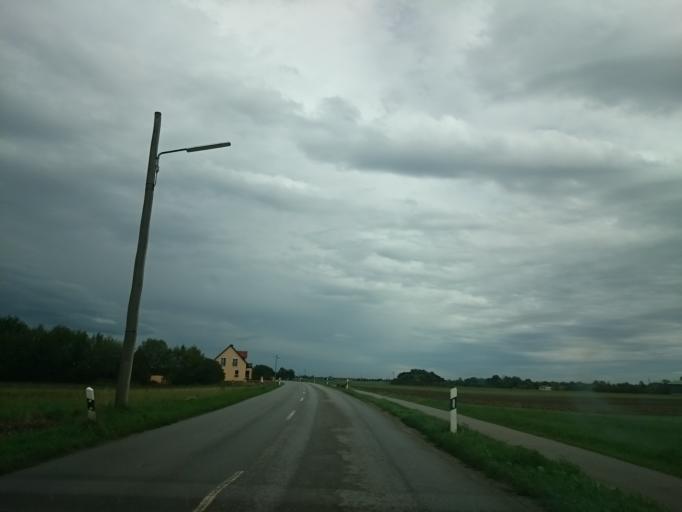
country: DE
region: Bavaria
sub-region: Swabia
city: Graben
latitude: 48.1933
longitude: 10.8232
